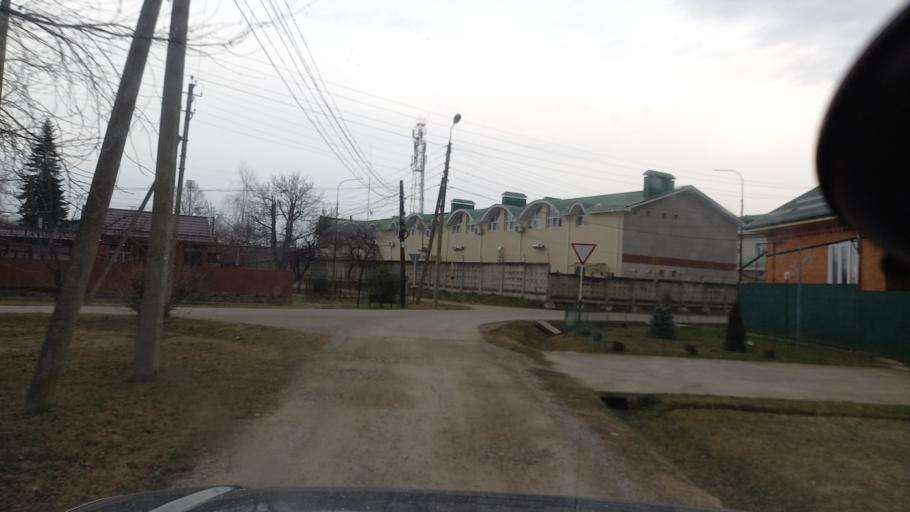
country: RU
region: Adygeya
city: Maykop
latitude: 44.5926
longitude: 40.1015
